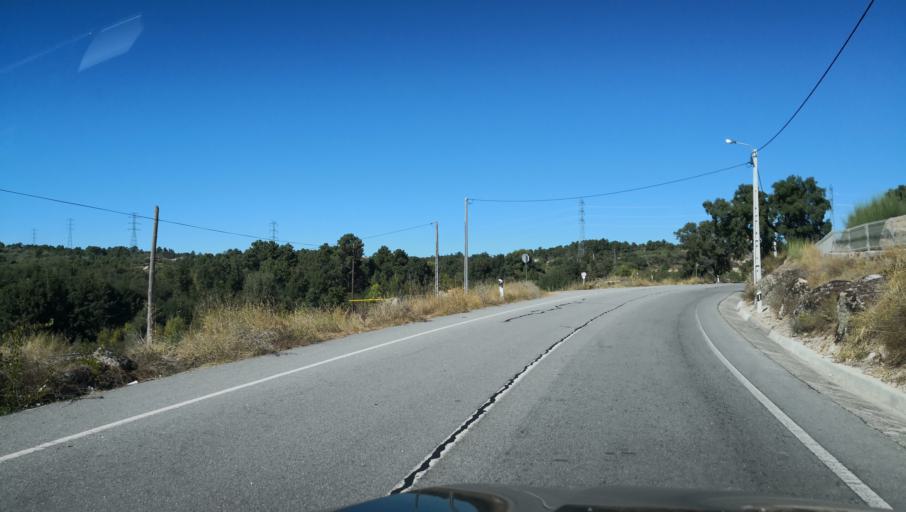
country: PT
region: Vila Real
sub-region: Valpacos
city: Valpacos
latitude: 41.6370
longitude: -7.3173
